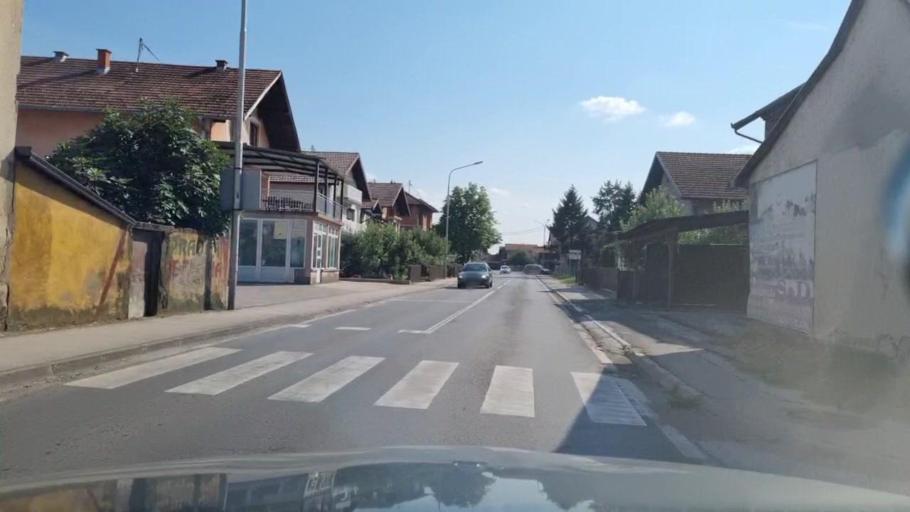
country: BA
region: Federation of Bosnia and Herzegovina
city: Odzak
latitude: 45.0107
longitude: 18.3282
